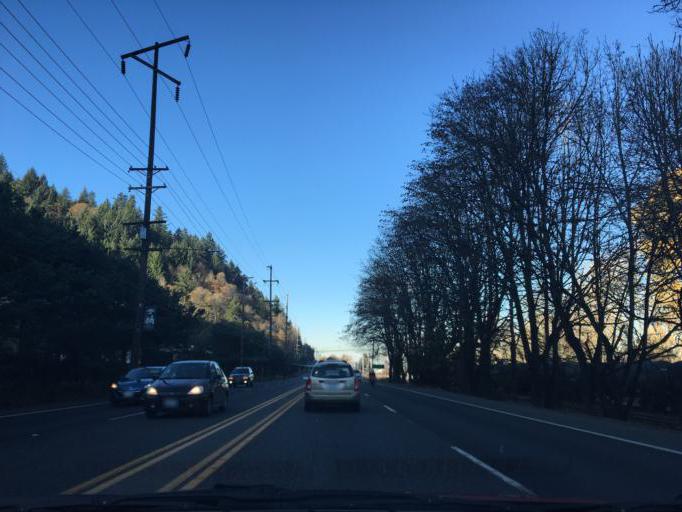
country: US
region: Oregon
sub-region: Washington County
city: West Haven
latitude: 45.5732
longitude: -122.7576
